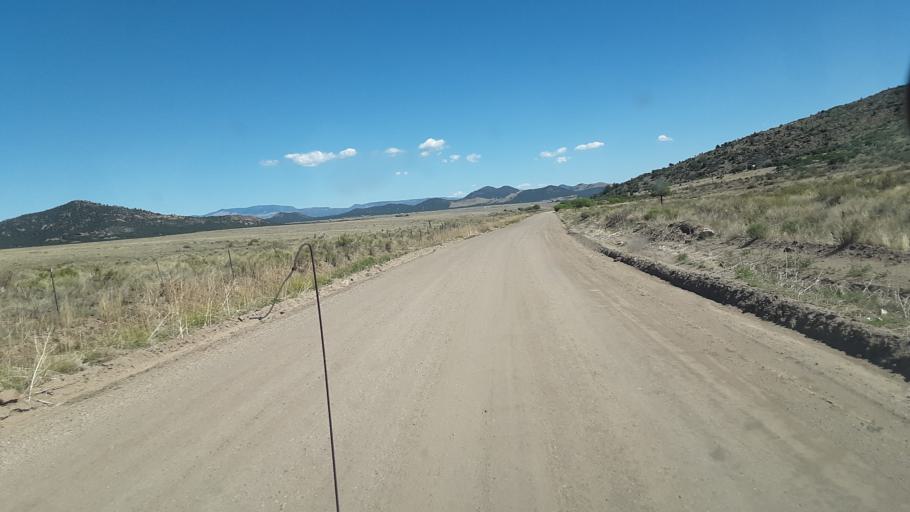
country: US
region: Colorado
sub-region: Custer County
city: Westcliffe
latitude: 38.2362
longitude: -105.5023
